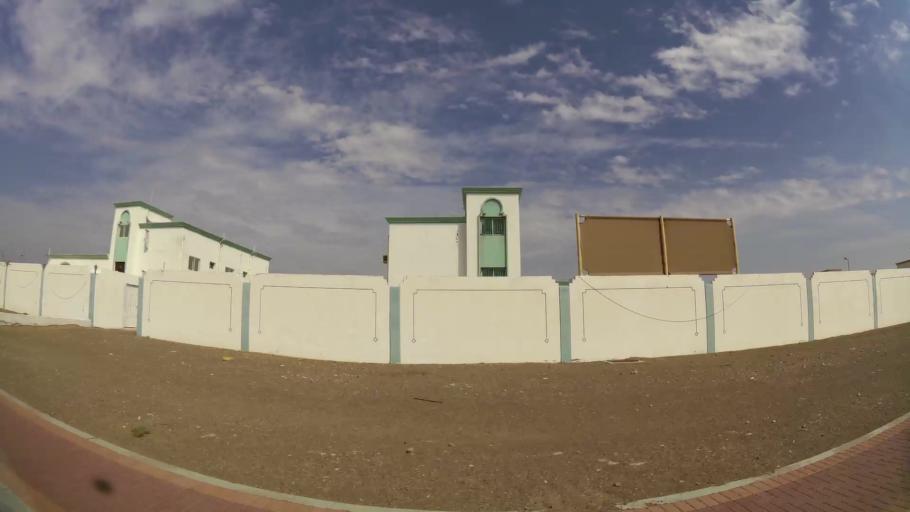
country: AE
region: Abu Dhabi
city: Al Ain
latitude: 24.1010
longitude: 55.8888
